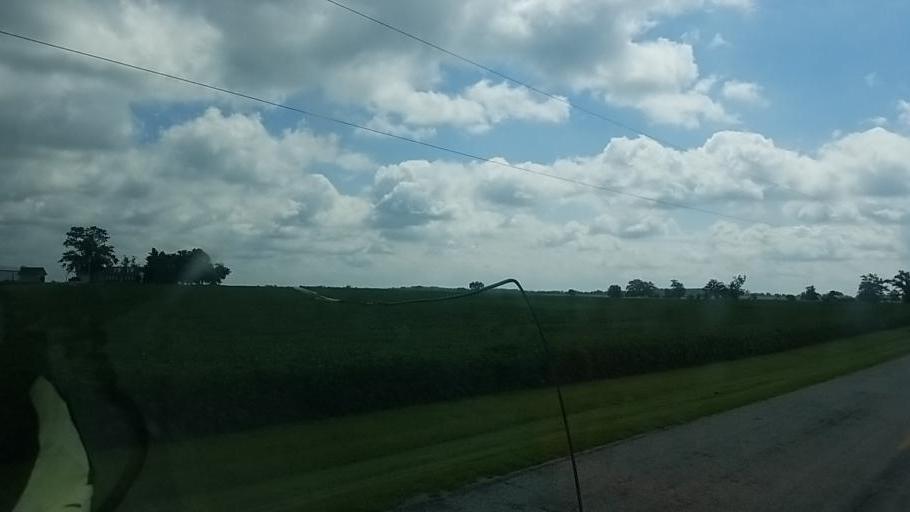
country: US
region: Ohio
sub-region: Madison County
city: Bethel
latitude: 39.7231
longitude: -83.4171
